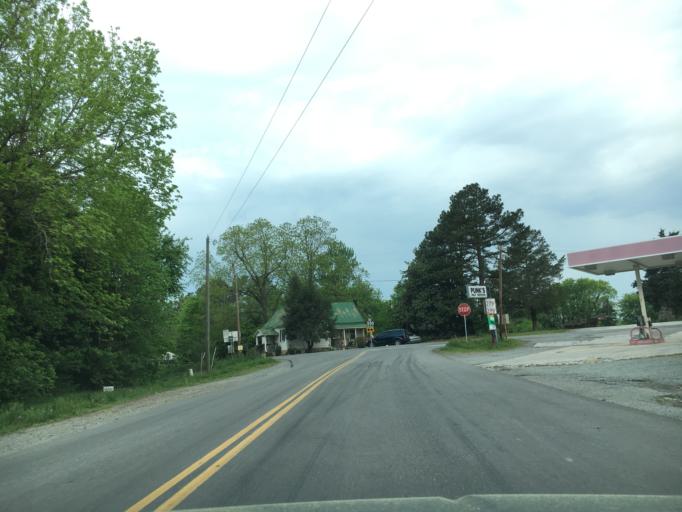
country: US
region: Virginia
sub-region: Campbell County
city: Brookneal
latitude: 36.9223
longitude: -78.9497
